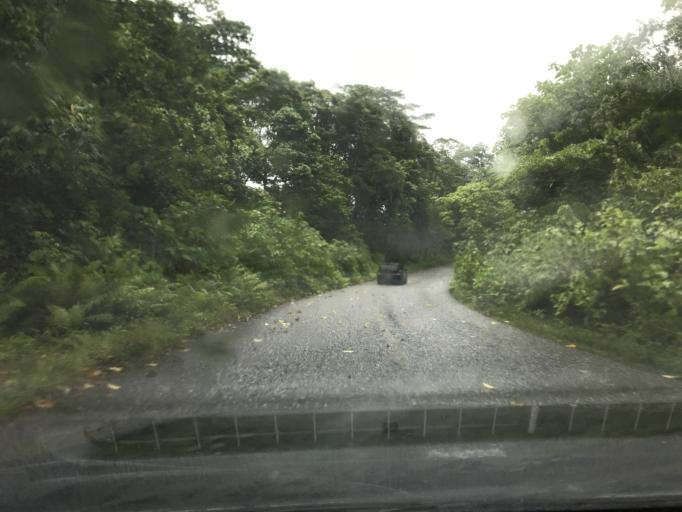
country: SB
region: Western Province
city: Gizo
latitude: -8.2740
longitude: 157.2406
